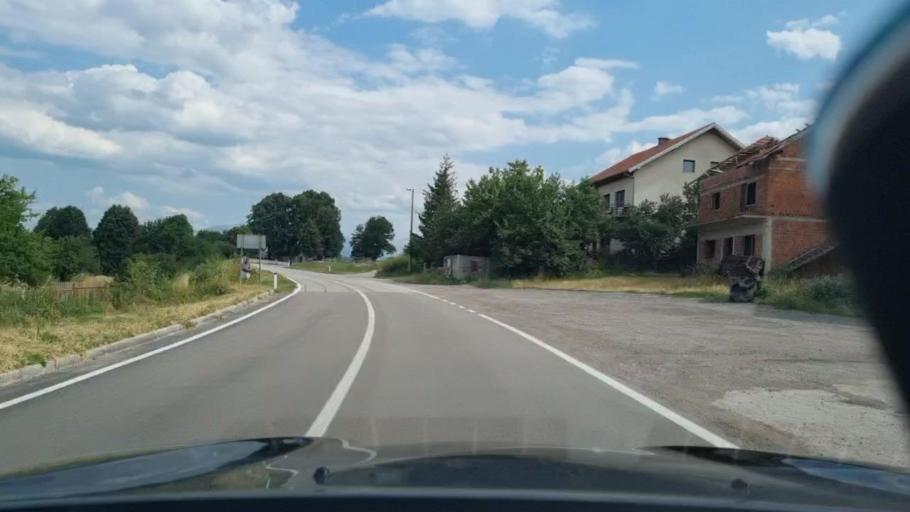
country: BA
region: Federation of Bosnia and Herzegovina
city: Bosansko Grahovo
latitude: 44.1732
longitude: 16.3717
